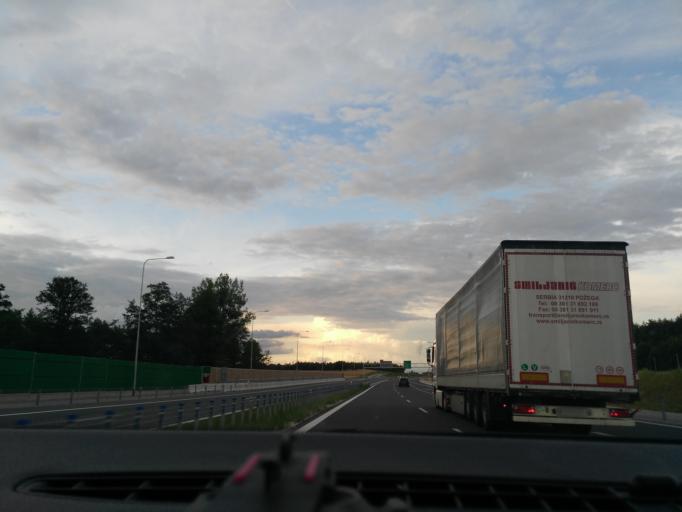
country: PL
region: Lublin Voivodeship
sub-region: Powiat lubelski
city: Jastkow
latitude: 51.2689
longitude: 22.4271
